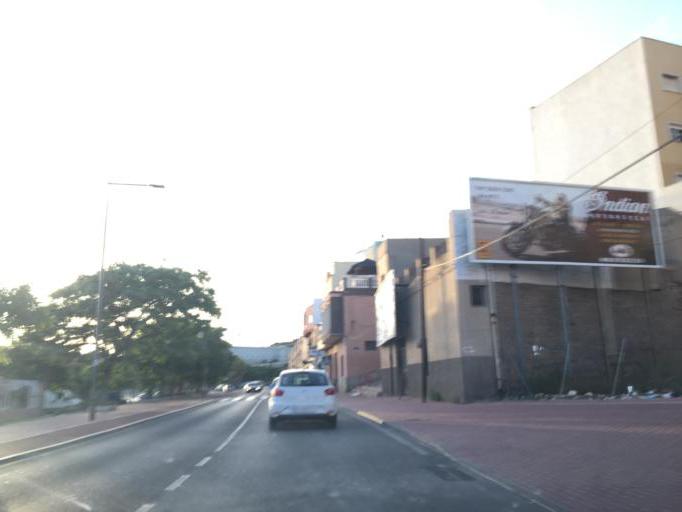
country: ES
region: Murcia
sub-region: Murcia
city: Cartagena
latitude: 37.5987
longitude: -0.9740
